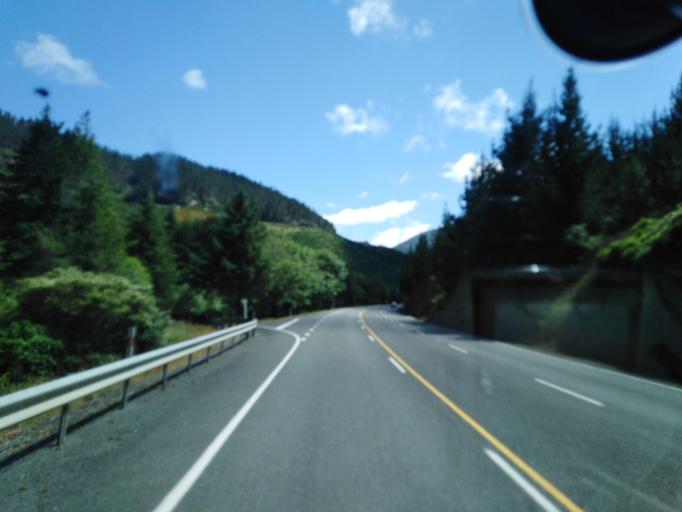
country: NZ
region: Nelson
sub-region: Nelson City
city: Nelson
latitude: -41.1815
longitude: 173.5595
